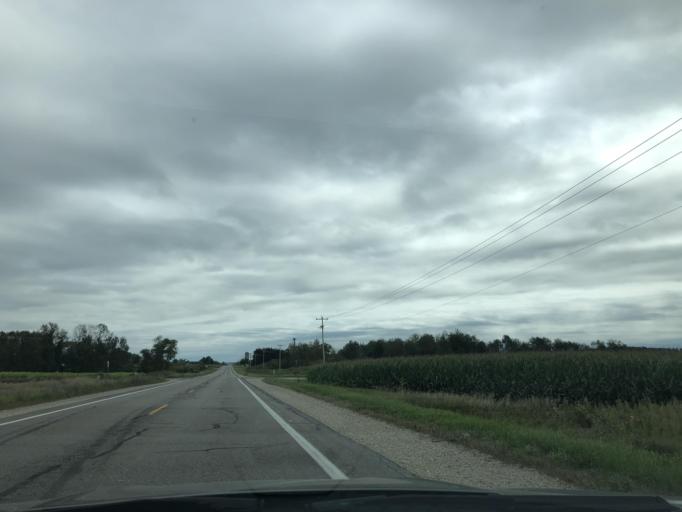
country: US
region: Michigan
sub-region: Missaukee County
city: Lake City
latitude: 44.1937
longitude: -85.1951
